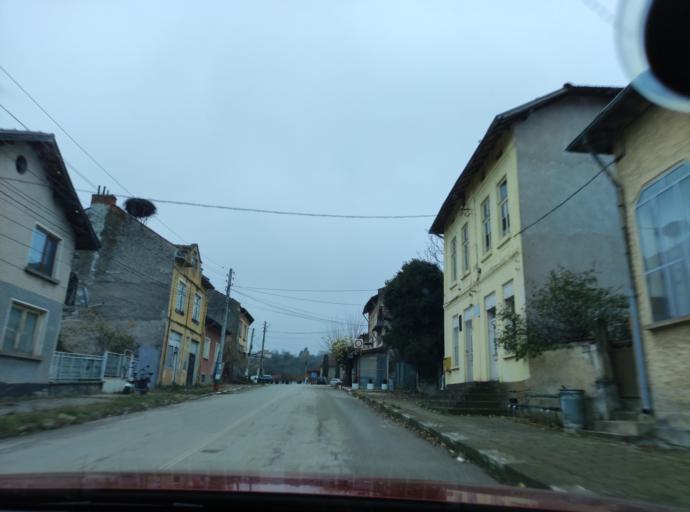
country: BG
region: Lovech
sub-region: Obshtina Yablanitsa
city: Yablanitsa
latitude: 43.0677
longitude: 24.0829
